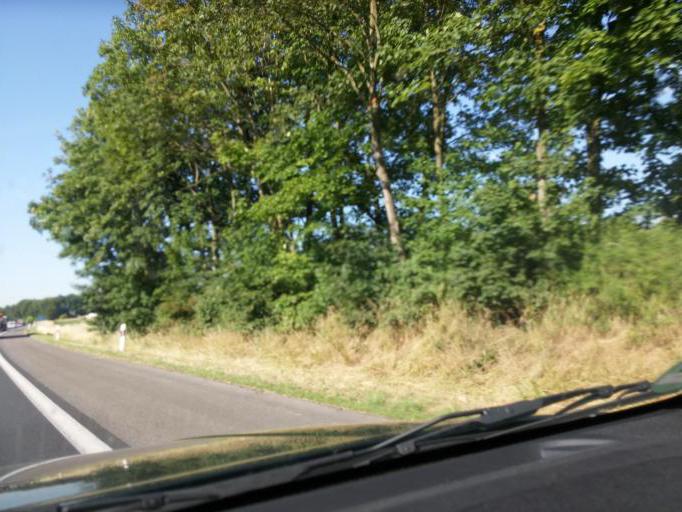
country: DE
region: North Rhine-Westphalia
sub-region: Regierungsbezirk Dusseldorf
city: Monchengladbach
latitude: 51.1710
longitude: 6.4047
